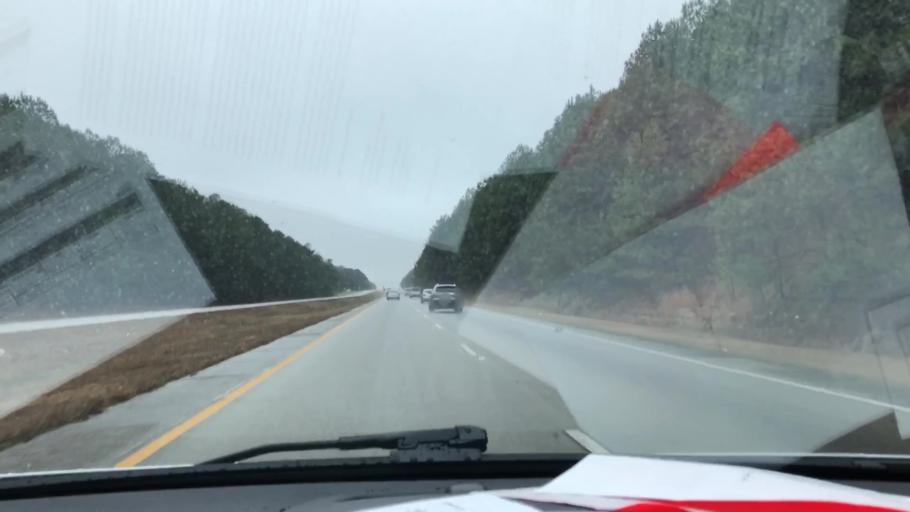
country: US
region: Georgia
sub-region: Barrow County
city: Auburn
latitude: 33.9596
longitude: -83.7893
